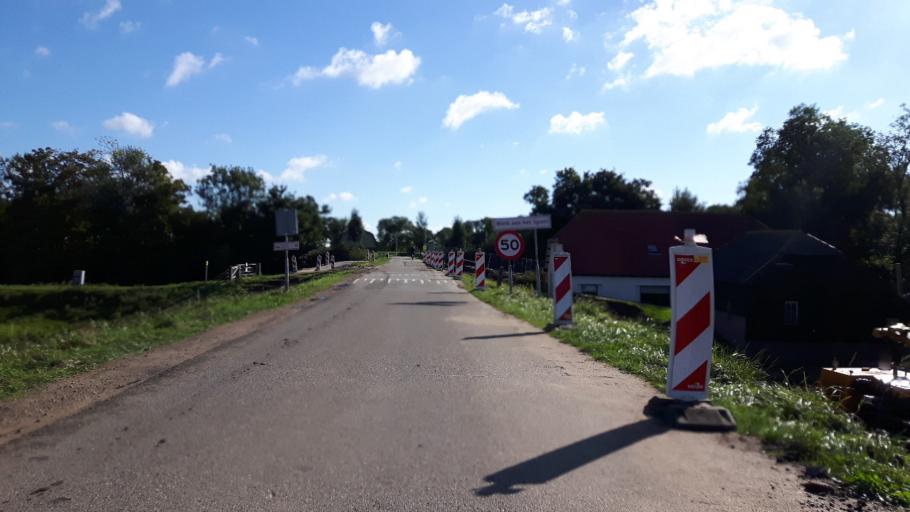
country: NL
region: Gelderland
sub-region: Gemeente Culemborg
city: Culemborg
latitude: 51.9592
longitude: 5.1882
